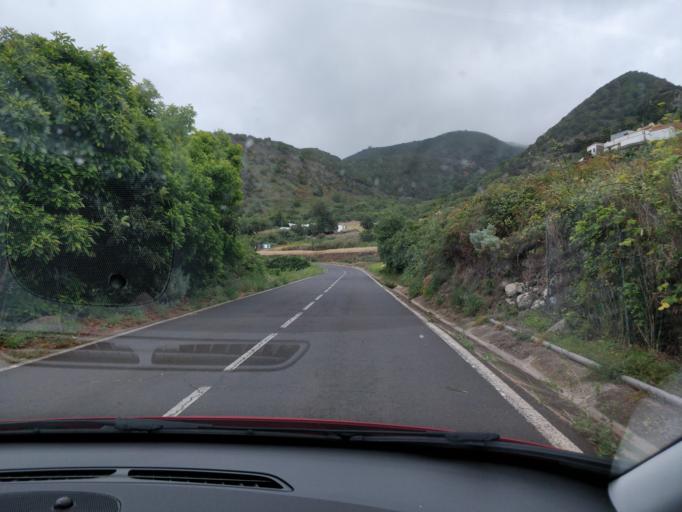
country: ES
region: Canary Islands
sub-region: Provincia de Santa Cruz de Tenerife
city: Tanque
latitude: 28.3341
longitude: -16.8457
